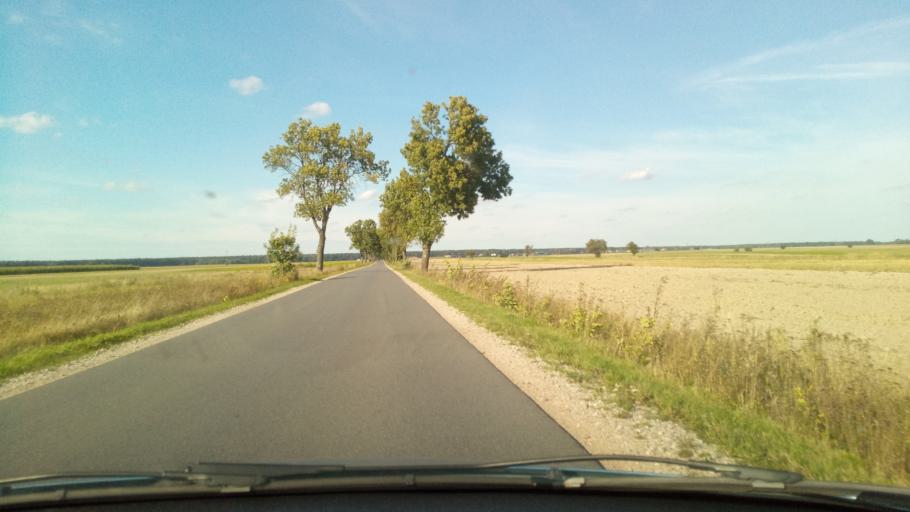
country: PL
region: Lodz Voivodeship
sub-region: Powiat piotrkowski
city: Sulejow
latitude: 51.3851
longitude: 19.8190
